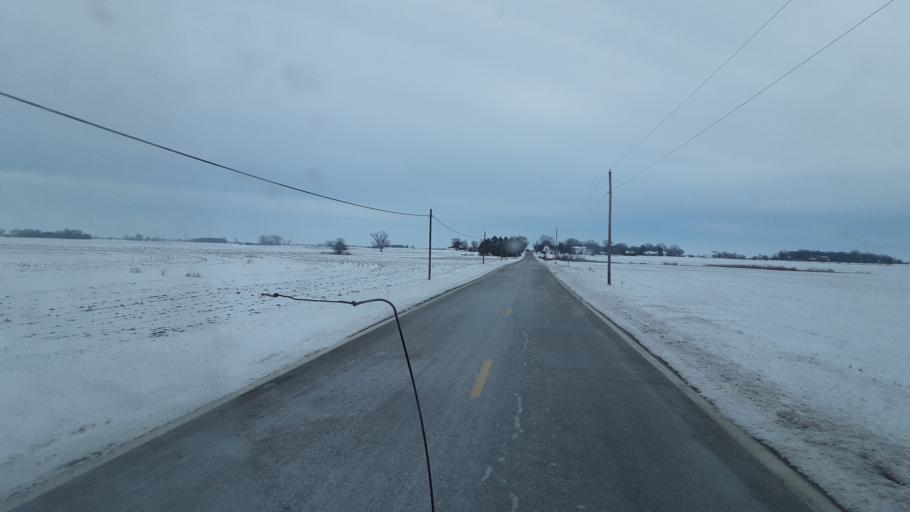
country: US
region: Ohio
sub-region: Madison County
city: Bethel
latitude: 39.7322
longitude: -83.4350
